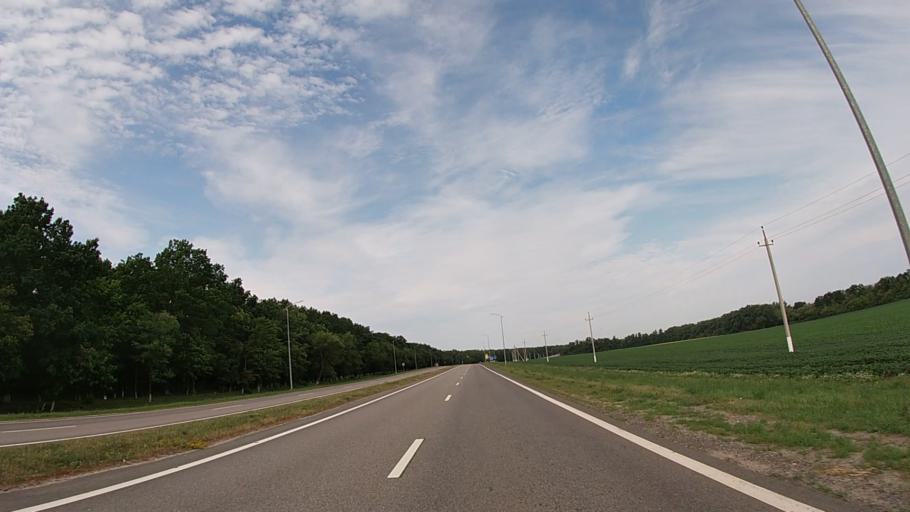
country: RU
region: Belgorod
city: Borisovka
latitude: 50.7540
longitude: 36.0220
